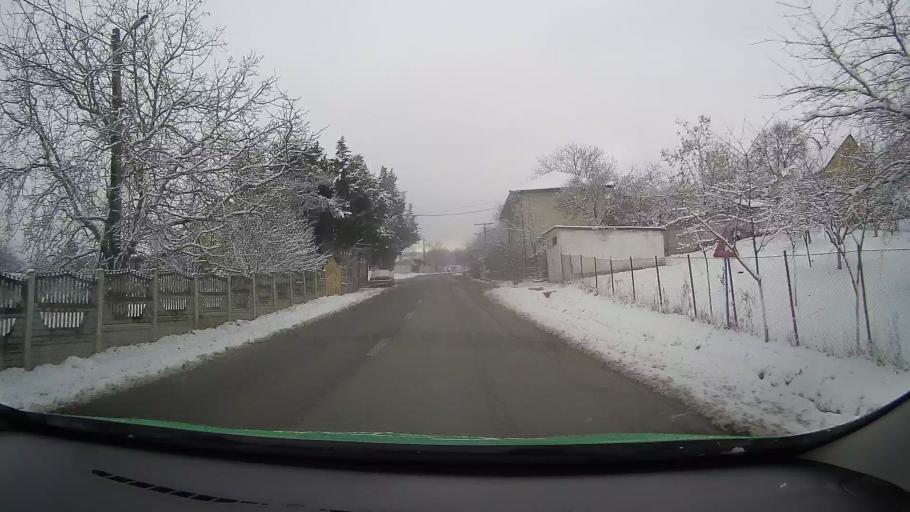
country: RO
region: Hunedoara
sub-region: Oras Hateg
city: Hateg
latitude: 45.6513
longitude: 22.9266
